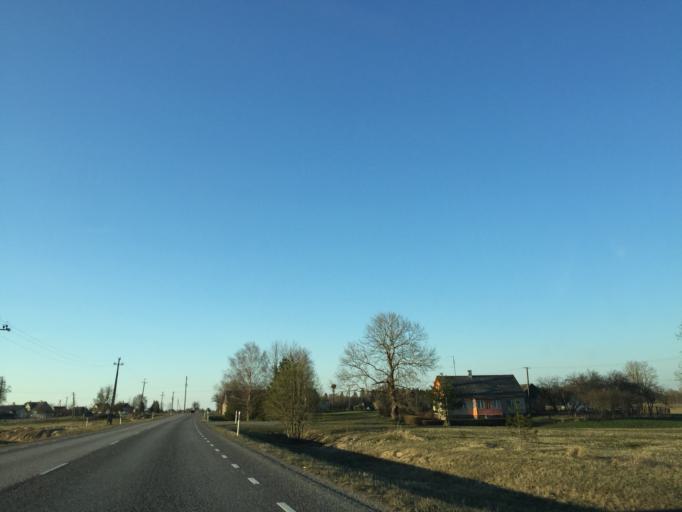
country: EE
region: Ida-Virumaa
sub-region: Johvi vald
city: Johvi
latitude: 59.2984
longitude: 27.4951
